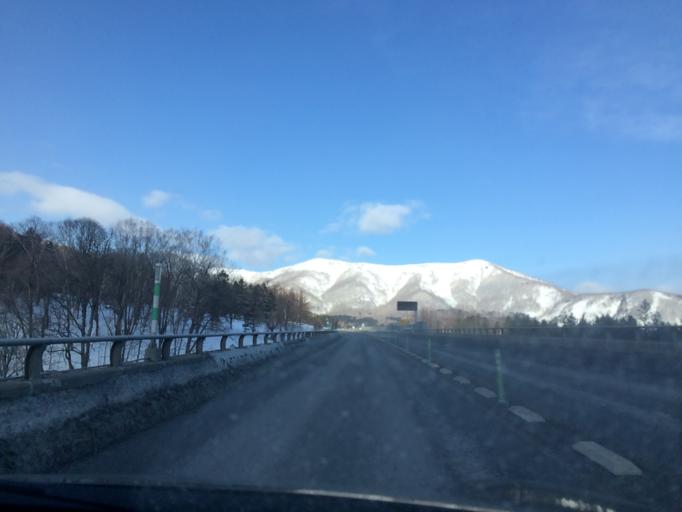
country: JP
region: Hokkaido
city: Otofuke
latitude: 43.0610
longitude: 142.7772
